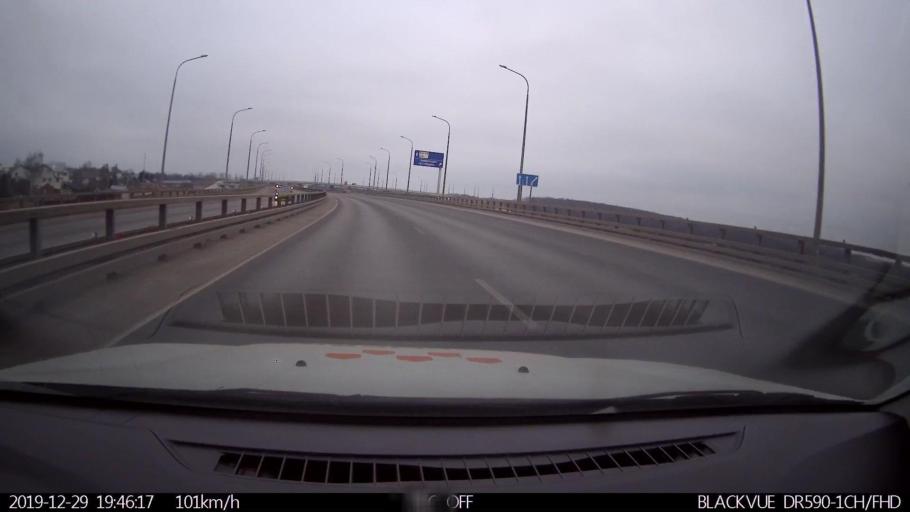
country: RU
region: Nizjnij Novgorod
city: Neklyudovo
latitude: 56.3932
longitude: 43.9829
